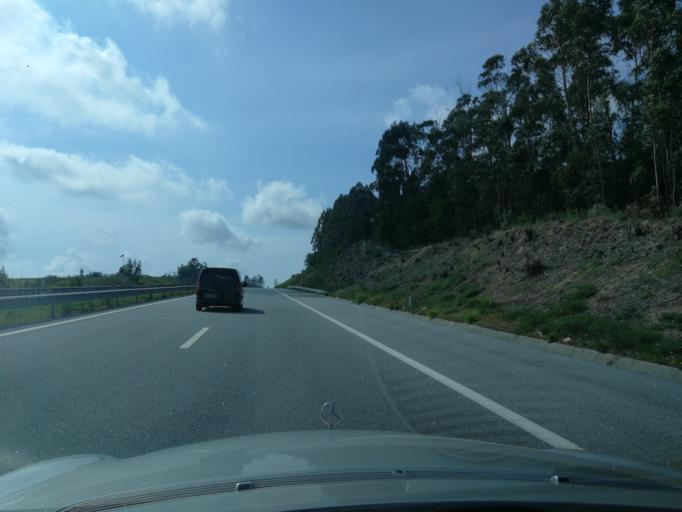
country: PT
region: Porto
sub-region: Vila do Conde
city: Arvore
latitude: 41.3806
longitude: -8.6498
